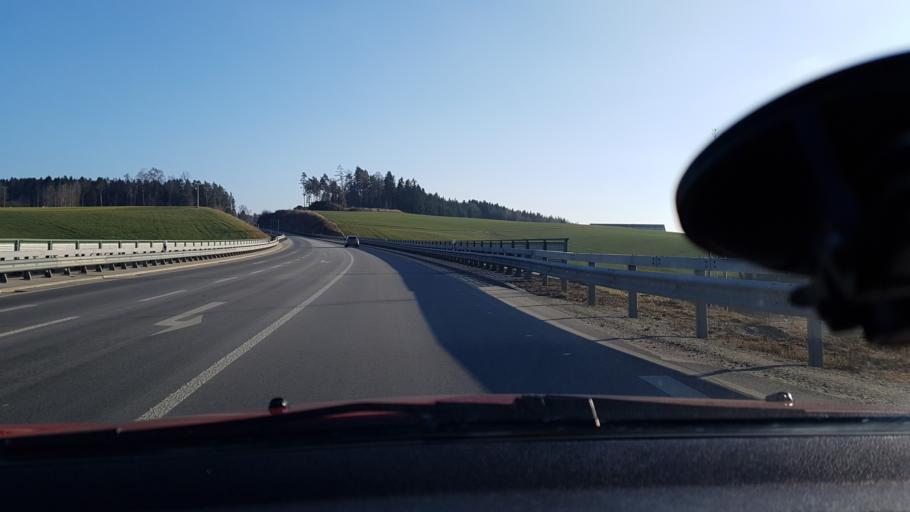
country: DE
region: Bavaria
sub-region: Lower Bavaria
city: Wittibreut
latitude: 48.3720
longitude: 12.9535
